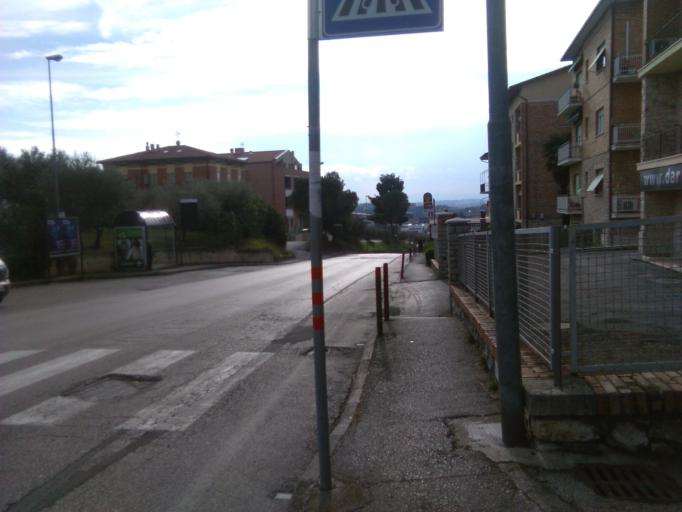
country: IT
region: Umbria
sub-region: Provincia di Perugia
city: Perugia
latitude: 43.0973
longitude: 12.3639
